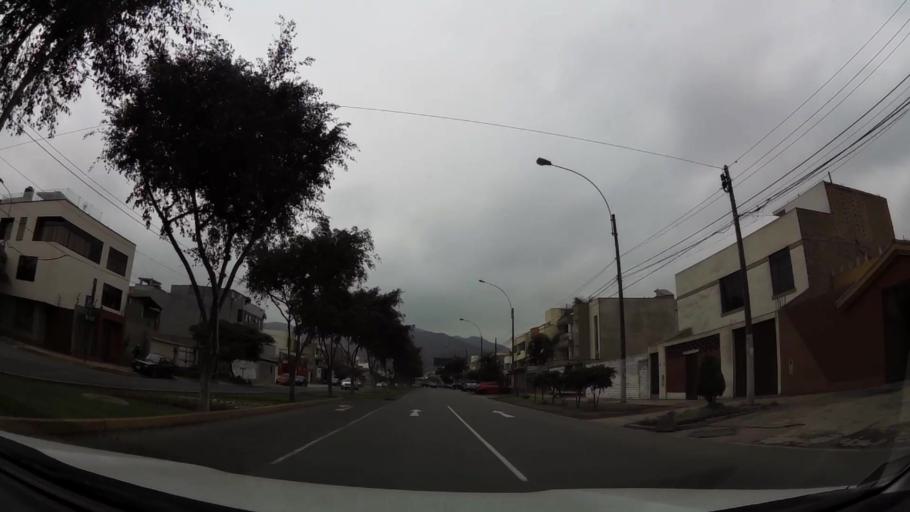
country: PE
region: Lima
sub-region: Lima
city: La Molina
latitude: -12.0731
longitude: -76.9477
